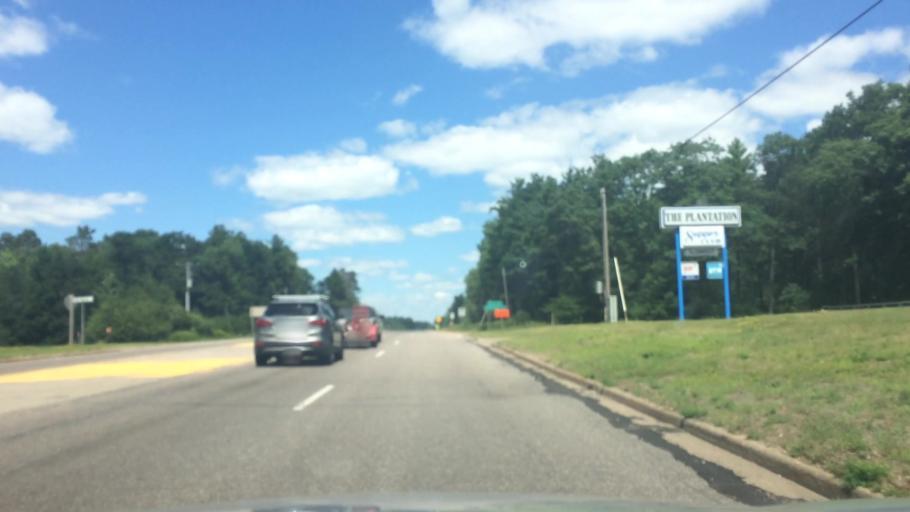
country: US
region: Wisconsin
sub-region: Vilas County
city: Lac du Flambeau
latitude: 45.9212
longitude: -89.6954
